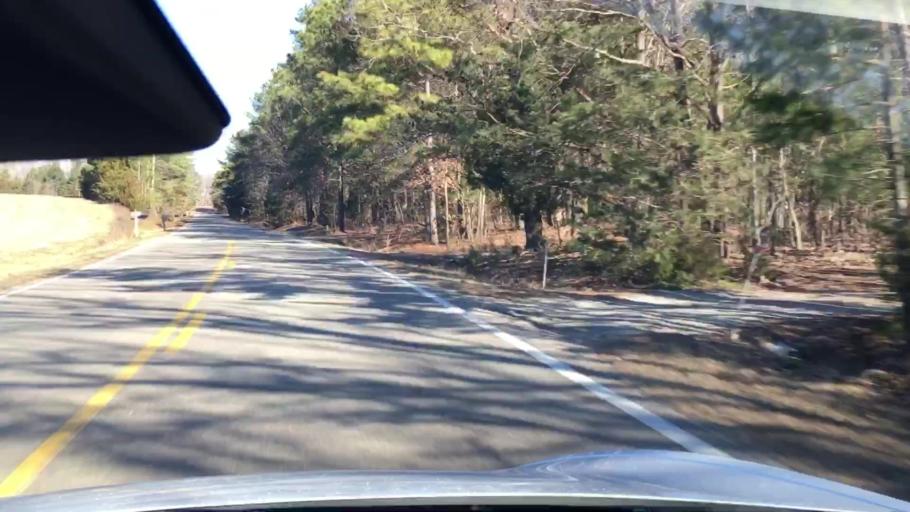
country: US
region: Virginia
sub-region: Powhatan County
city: Powhatan
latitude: 37.5356
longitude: -77.7986
